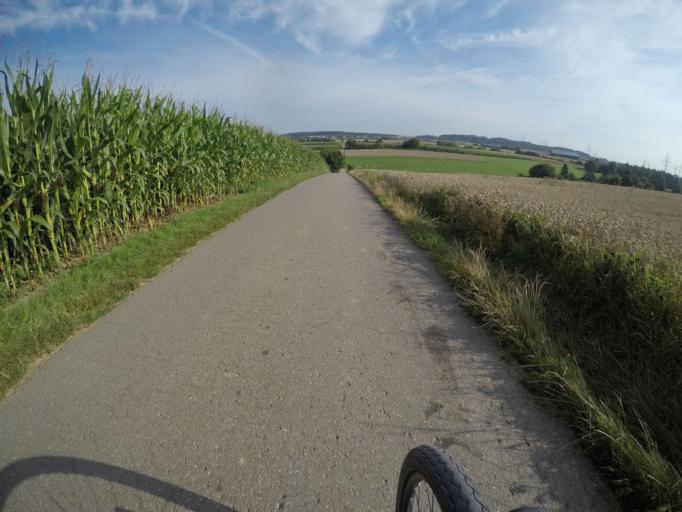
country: DE
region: Baden-Wuerttemberg
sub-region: Regierungsbezirk Stuttgart
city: Rutesheim
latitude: 48.7986
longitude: 8.9767
